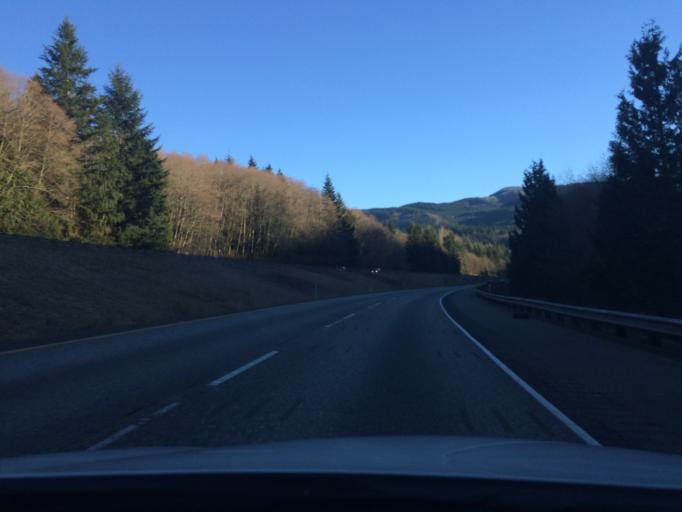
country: US
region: Washington
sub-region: Whatcom County
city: Geneva
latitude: 48.6900
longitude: -122.4150
